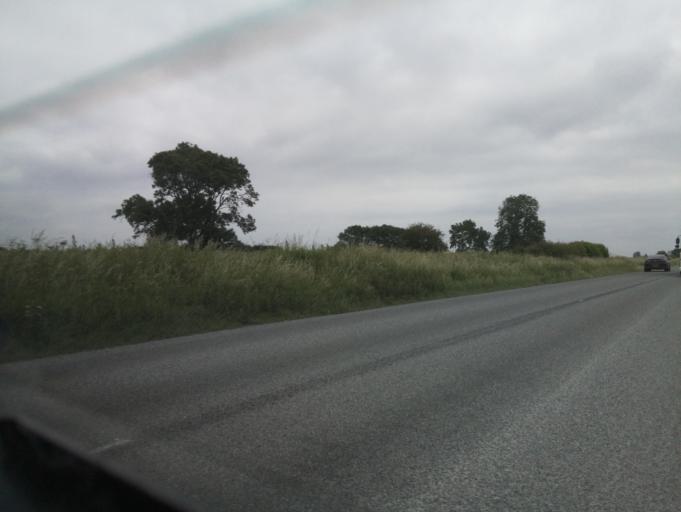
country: GB
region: England
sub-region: District of Rutland
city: Exton
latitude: 52.6710
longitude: -0.6448
